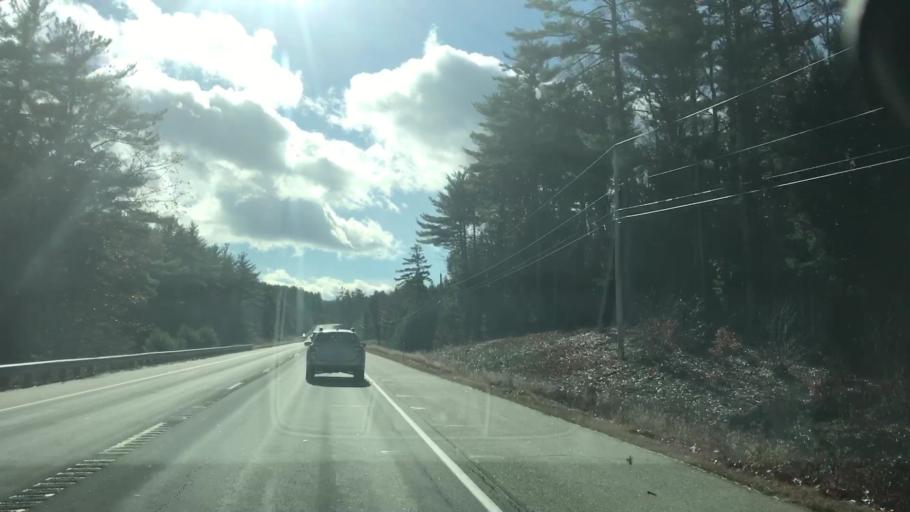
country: US
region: New Hampshire
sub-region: Carroll County
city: Wolfeboro
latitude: 43.5320
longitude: -71.2041
